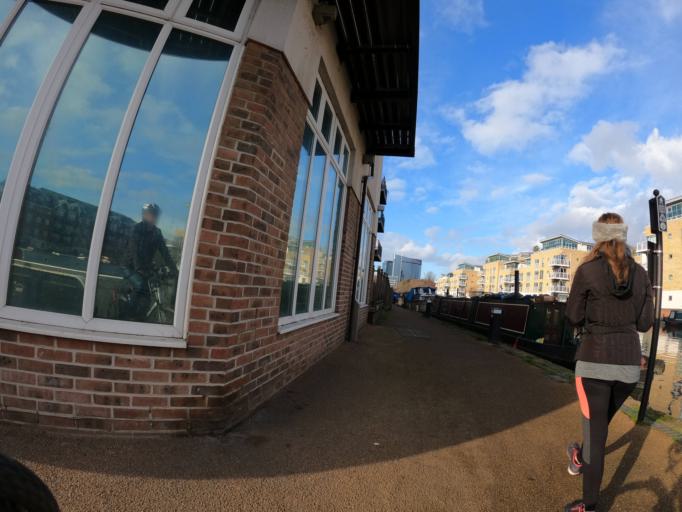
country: GB
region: England
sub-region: Greater London
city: Brentford
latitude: 51.4835
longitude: -0.3118
